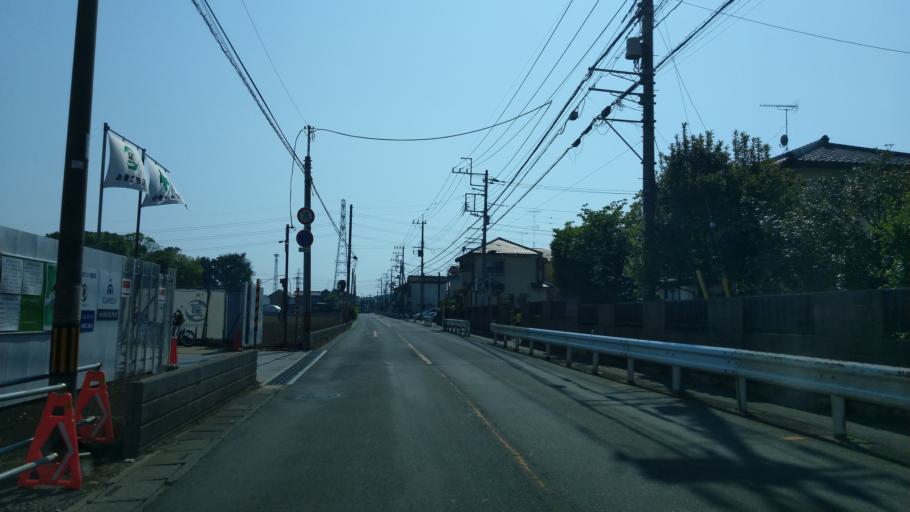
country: JP
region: Saitama
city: Oi
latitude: 35.8508
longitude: 139.5088
